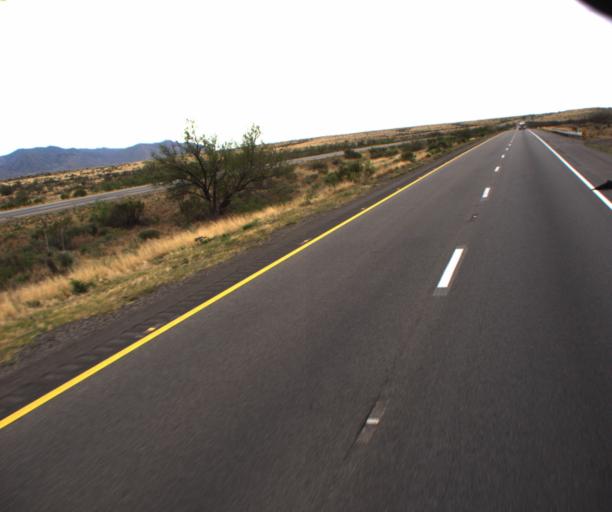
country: US
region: Arizona
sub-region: Cochise County
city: Willcox
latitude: 32.1023
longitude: -110.0301
